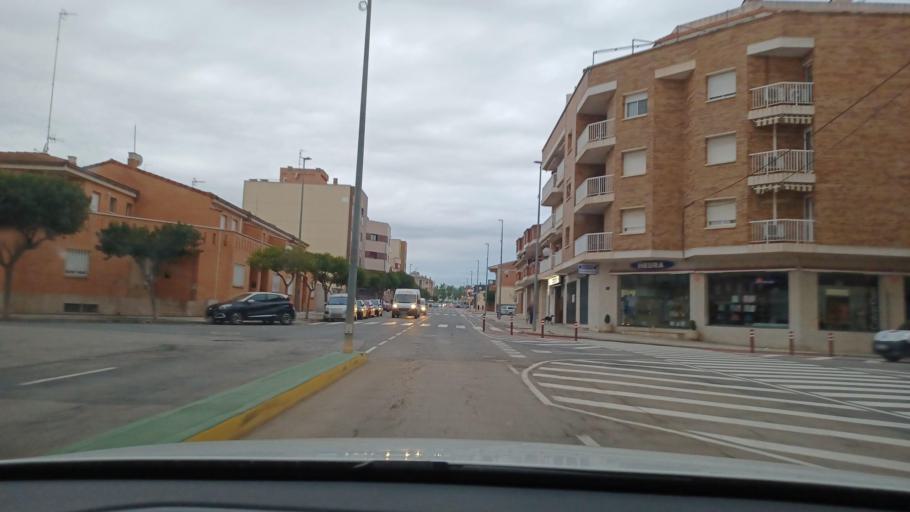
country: ES
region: Catalonia
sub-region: Provincia de Tarragona
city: Amposta
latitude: 40.7062
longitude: 0.5773
